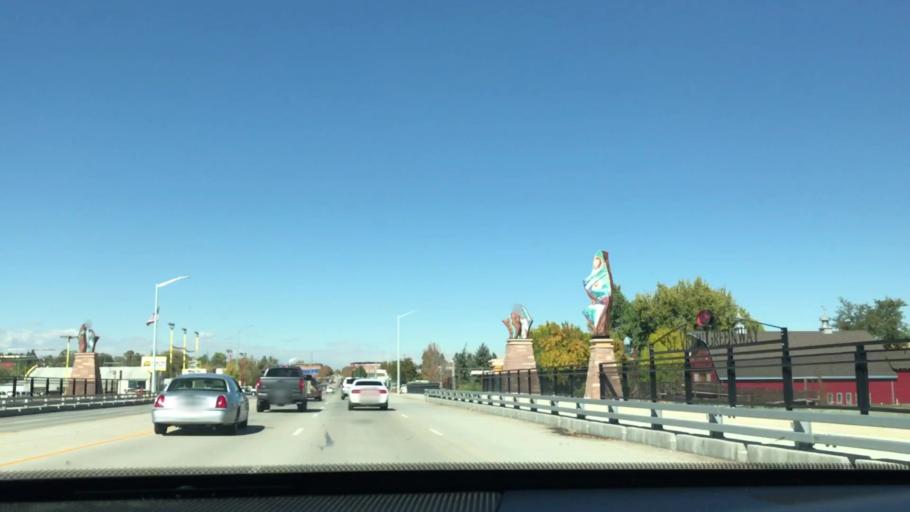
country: US
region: Colorado
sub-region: Boulder County
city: Longmont
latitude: 40.1555
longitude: -105.1025
